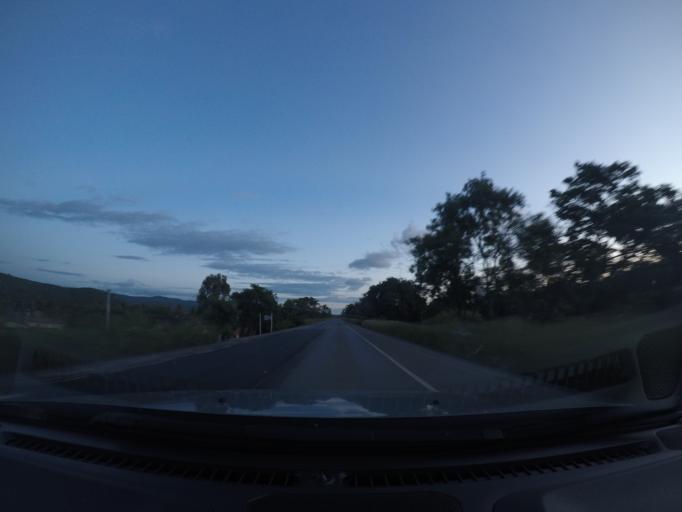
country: BR
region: Bahia
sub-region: Seabra
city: Seabra
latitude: -12.4759
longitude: -41.7405
